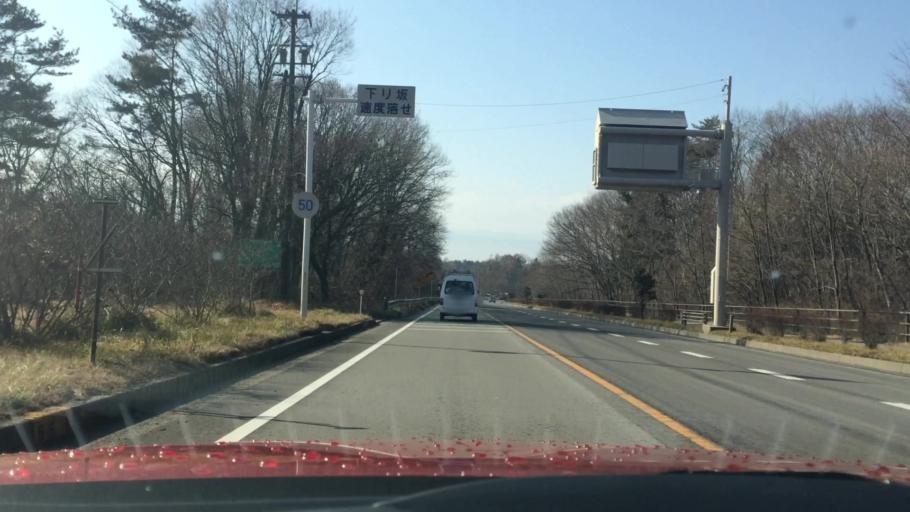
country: JP
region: Nagano
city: Komoro
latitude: 36.3321
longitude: 138.5231
